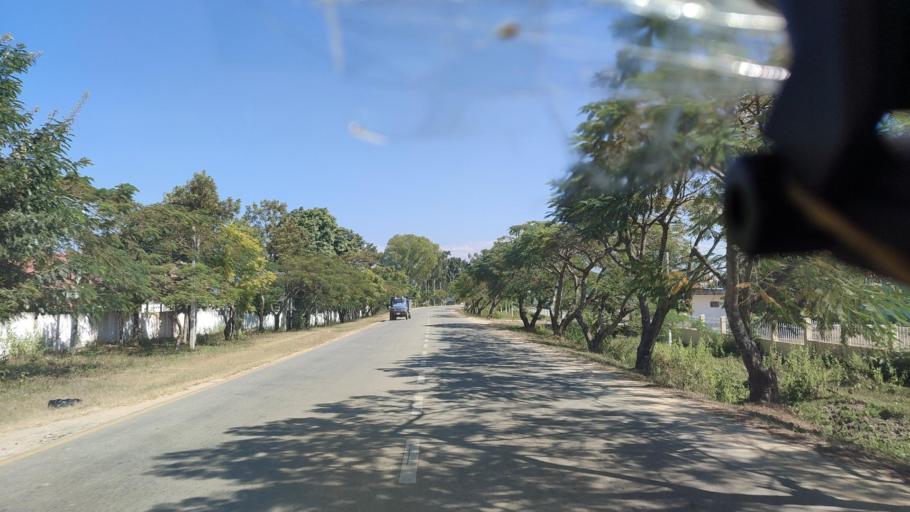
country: TH
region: Chiang Rai
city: Mae Sai
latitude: 21.2877
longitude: 99.5780
